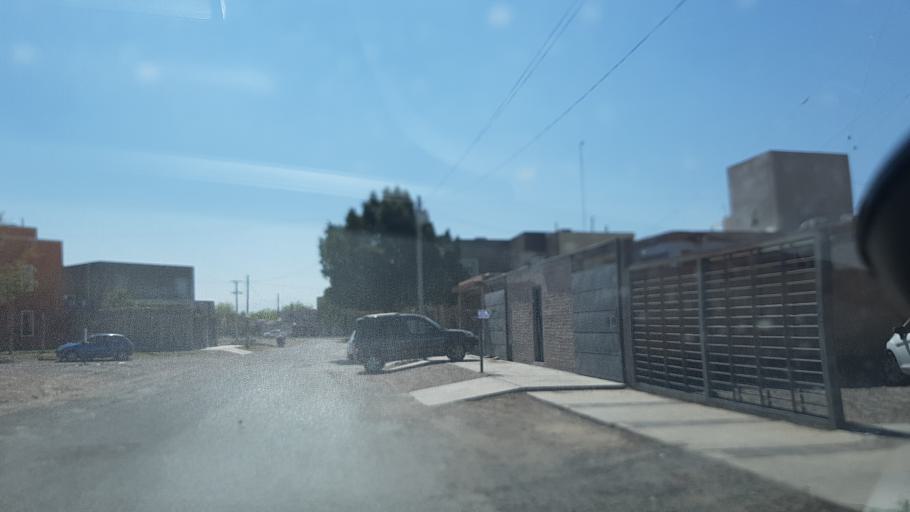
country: AR
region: San Juan
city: San Juan
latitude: -31.5213
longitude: -68.5893
